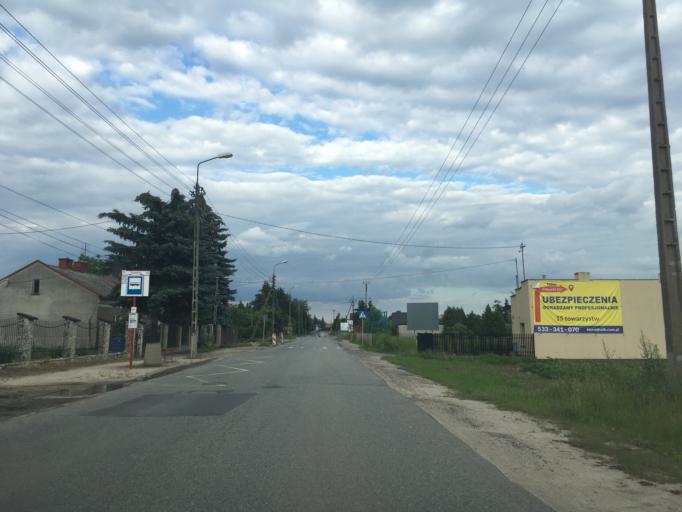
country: PL
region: Masovian Voivodeship
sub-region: Powiat piaseczynski
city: Mysiadlo
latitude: 52.1102
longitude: 21.0048
